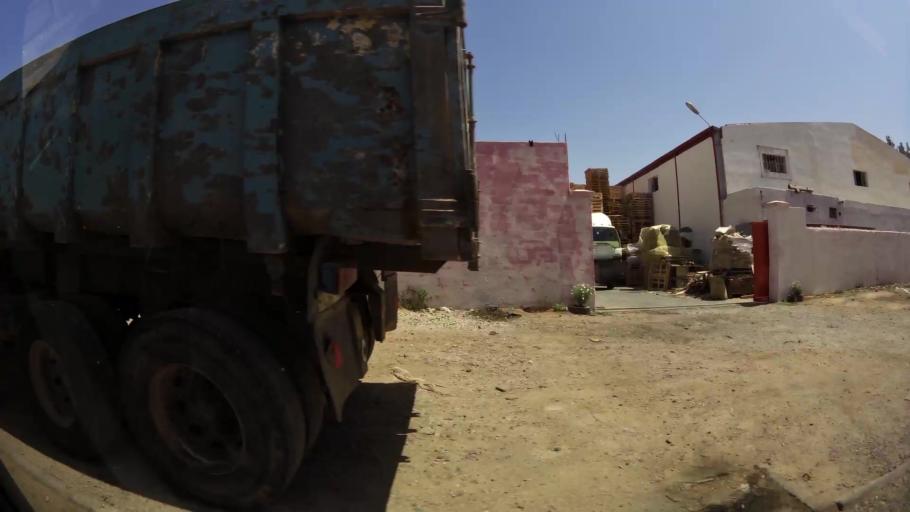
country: MA
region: Souss-Massa-Draa
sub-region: Inezgane-Ait Mellou
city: Inezgane
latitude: 30.3365
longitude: -9.4877
